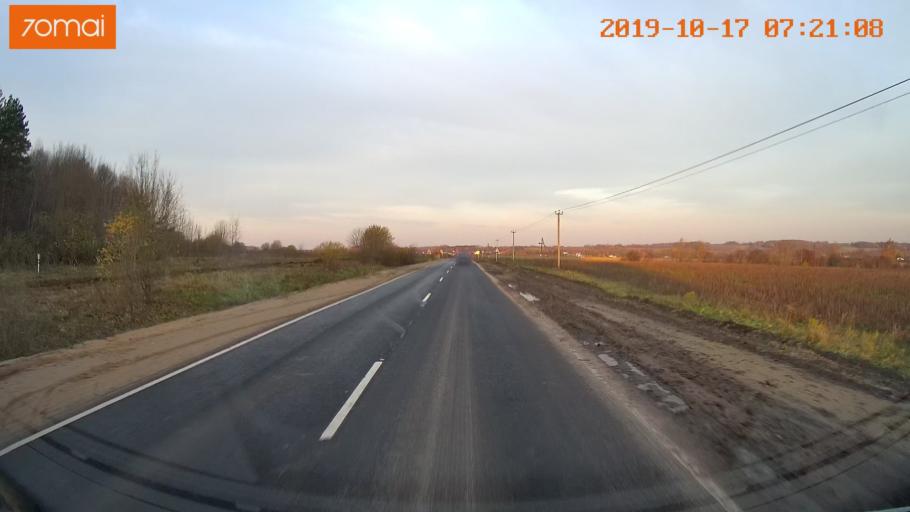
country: RU
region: Ivanovo
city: Gavrilov Posad
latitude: 56.3455
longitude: 40.1685
